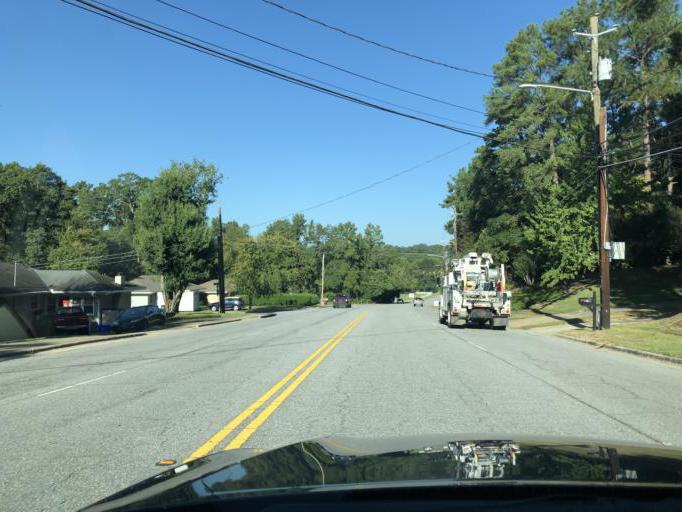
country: US
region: Georgia
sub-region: Muscogee County
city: Columbus
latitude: 32.4909
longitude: -84.9385
